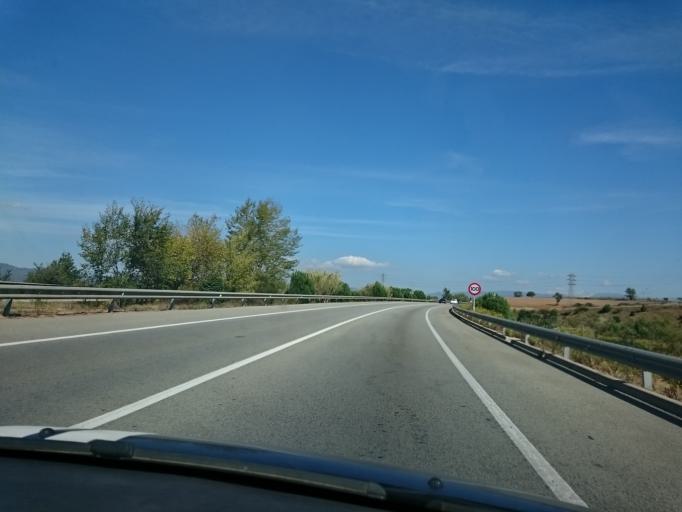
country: ES
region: Catalonia
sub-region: Provincia de Barcelona
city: Santa Perpetua de Mogoda
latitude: 41.5582
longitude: 2.1855
